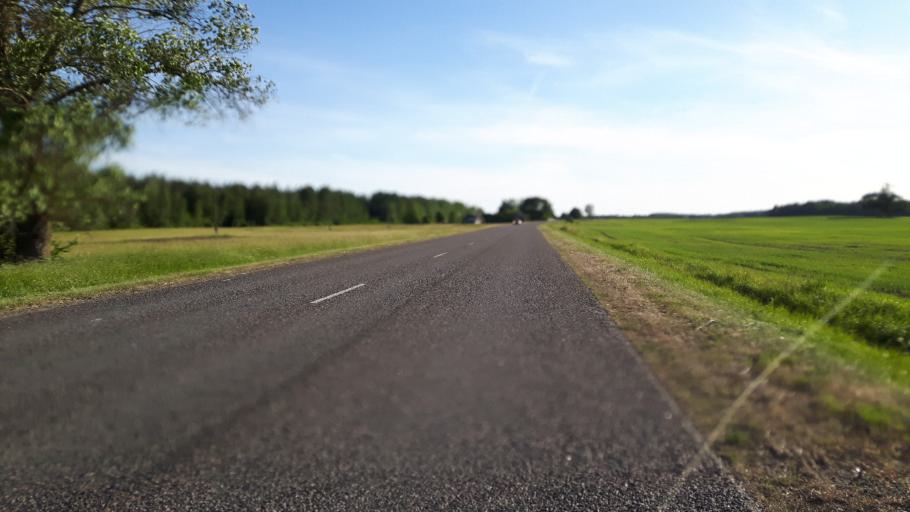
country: LV
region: Kuldigas Rajons
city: Kuldiga
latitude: 57.0249
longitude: 22.1828
